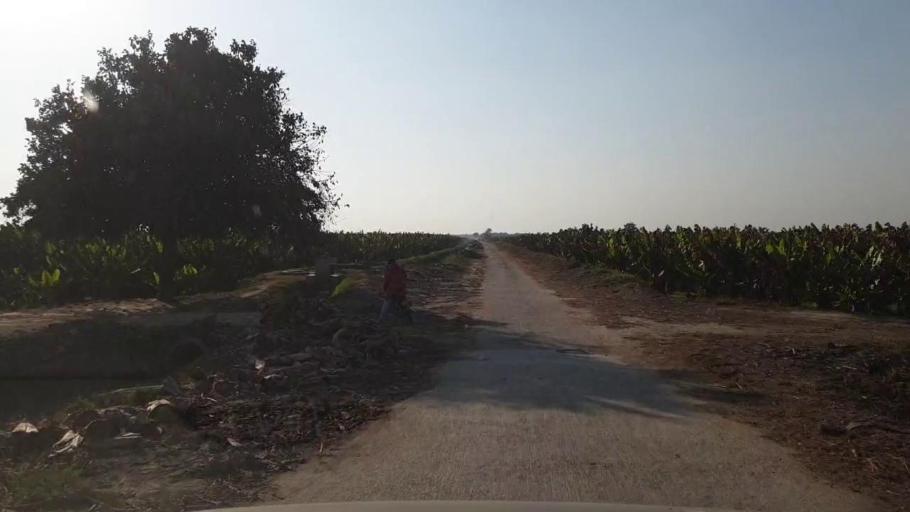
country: PK
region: Sindh
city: Tando Allahyar
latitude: 25.3467
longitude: 68.6740
